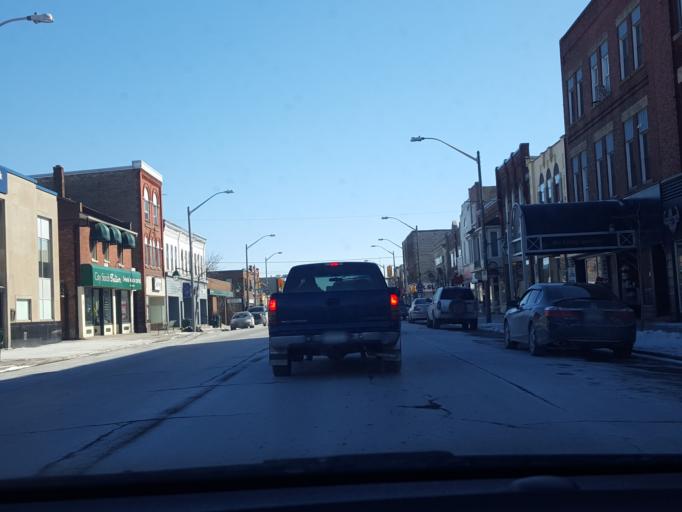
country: CA
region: Ontario
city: Cambridge
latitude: 43.3965
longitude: -80.3596
